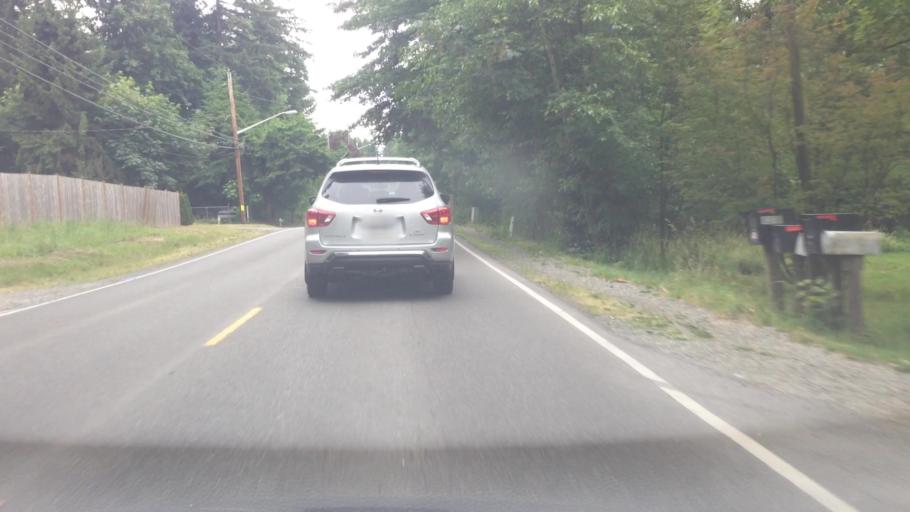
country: US
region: Washington
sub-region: Pierce County
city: South Hill
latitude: 47.1229
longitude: -122.3041
